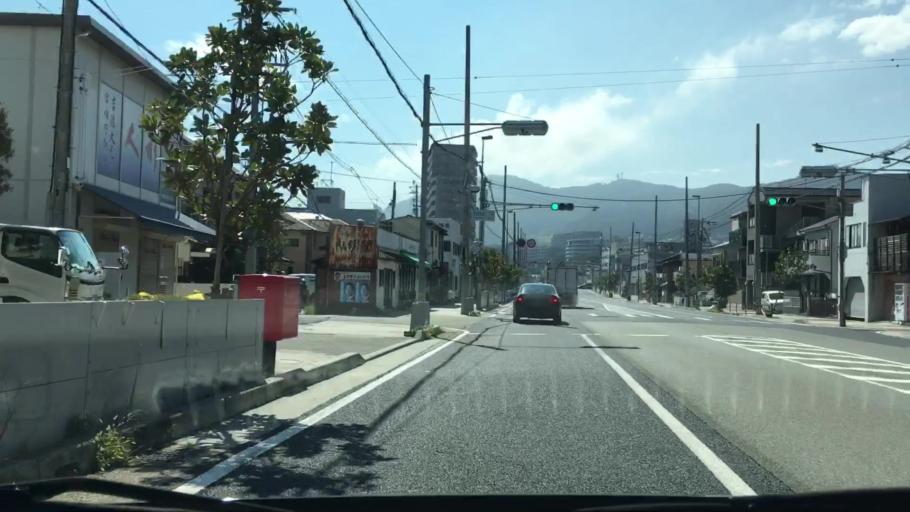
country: JP
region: Hyogo
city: Kobe
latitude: 34.6438
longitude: 135.1179
